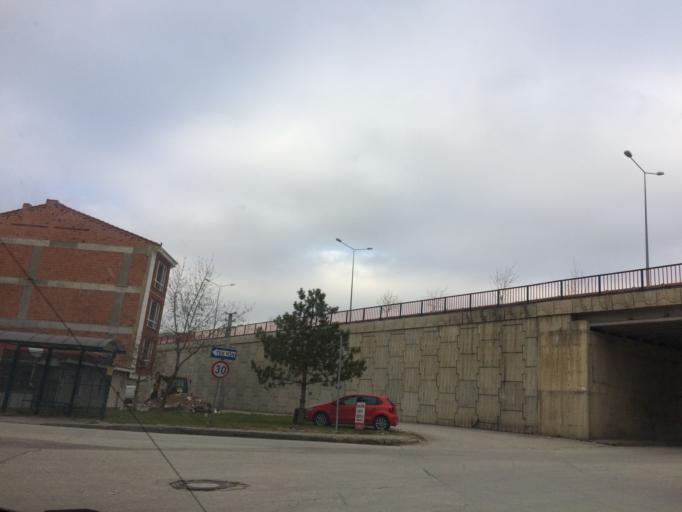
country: TR
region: Eskisehir
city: Eskisehir
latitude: 39.7790
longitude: 30.4837
